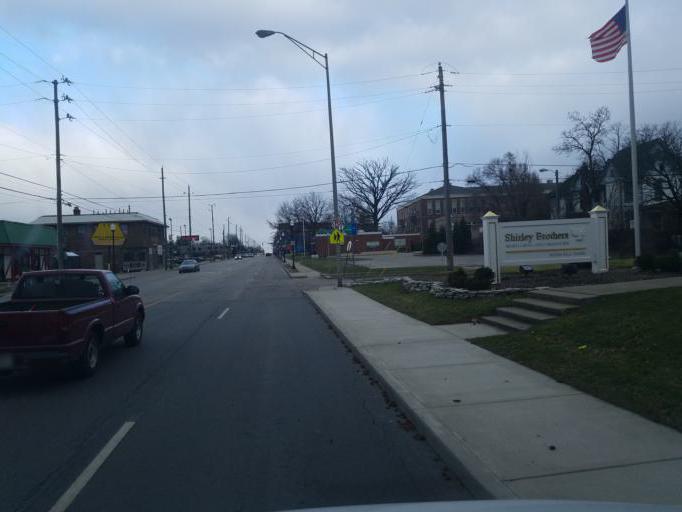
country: US
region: Indiana
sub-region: Marion County
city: Warren Park
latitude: 39.7705
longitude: -86.0763
